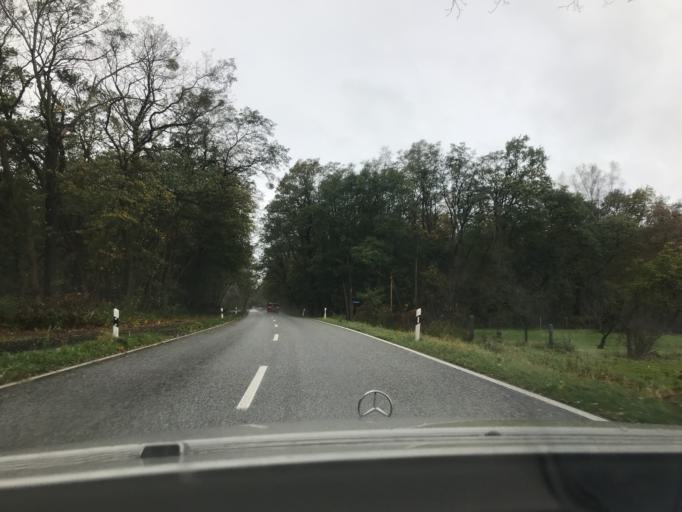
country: DE
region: Brandenburg
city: Trebbin
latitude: 52.2109
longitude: 13.1284
